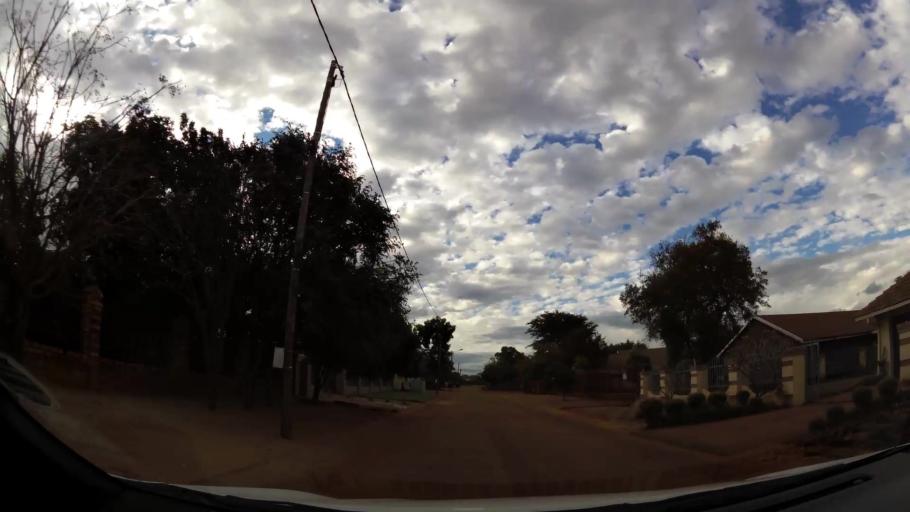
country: ZA
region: Limpopo
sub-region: Waterberg District Municipality
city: Modimolle
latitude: -24.5079
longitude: 28.7247
